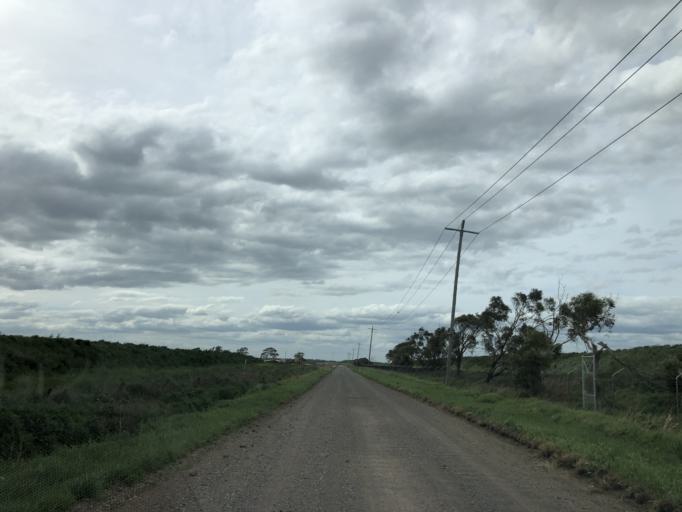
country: AU
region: Victoria
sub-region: Kingston
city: Patterson Lakes
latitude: -38.0741
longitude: 145.1660
